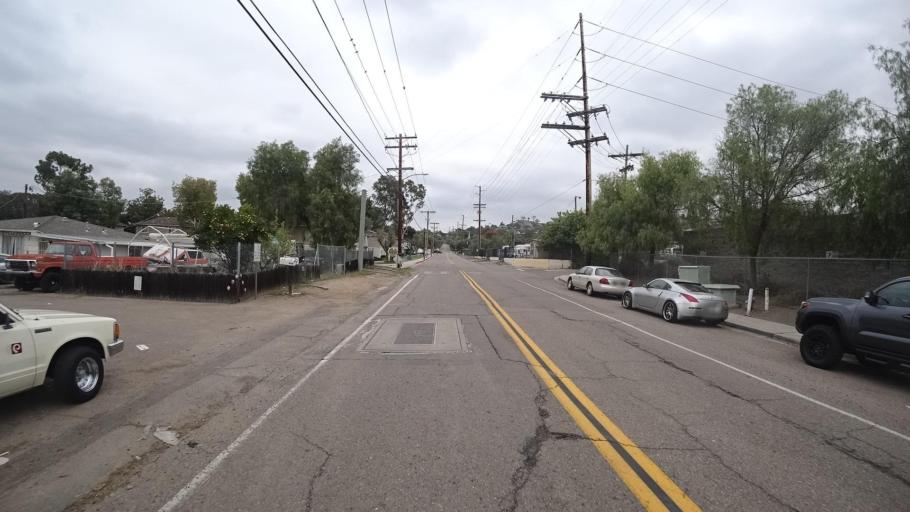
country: US
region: California
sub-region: San Diego County
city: Spring Valley
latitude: 32.7395
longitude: -117.0028
